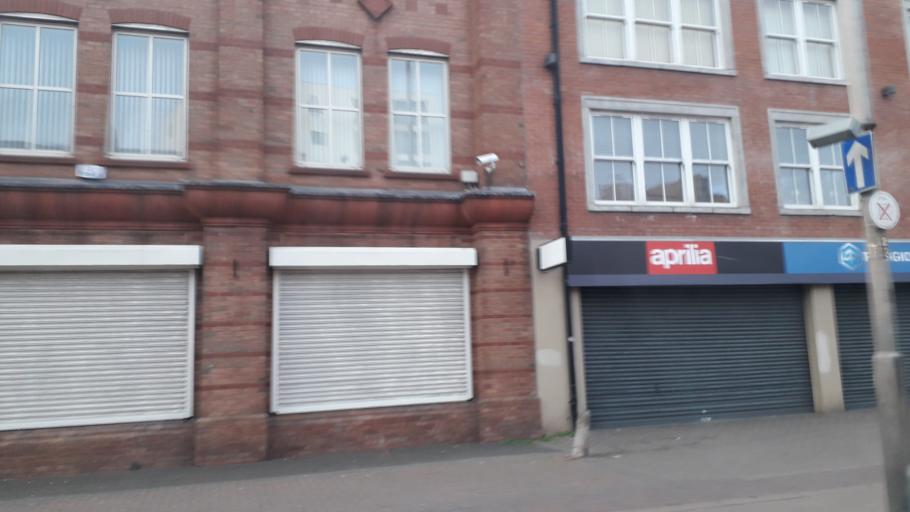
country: GB
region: Northern Ireland
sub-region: City of Belfast
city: Belfast
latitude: 54.5912
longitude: -5.9342
